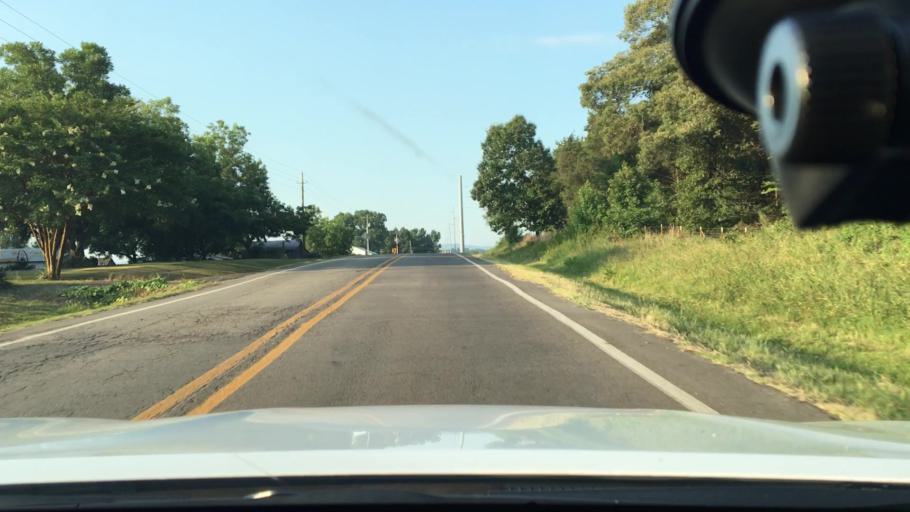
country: US
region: Arkansas
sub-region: Johnson County
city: Coal Hill
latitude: 35.3772
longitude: -93.5613
